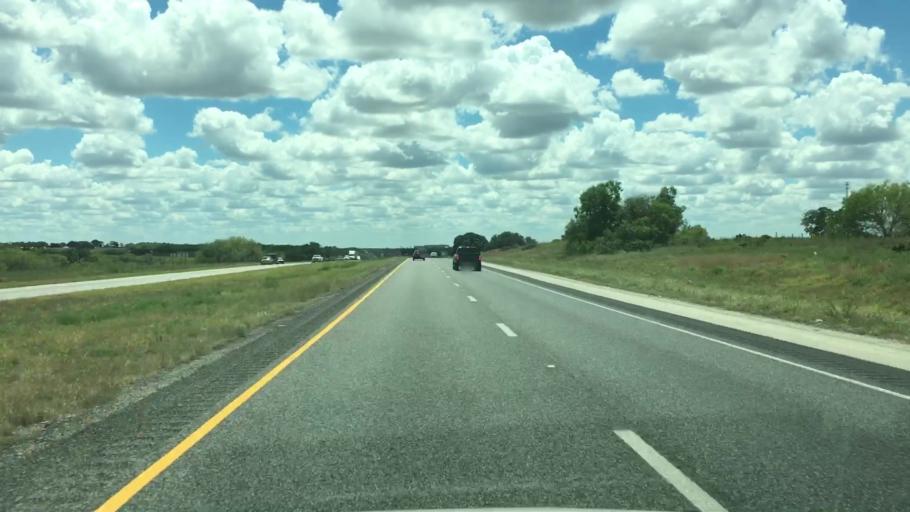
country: US
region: Texas
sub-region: Atascosa County
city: Poteet
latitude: 29.1214
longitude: -98.4314
